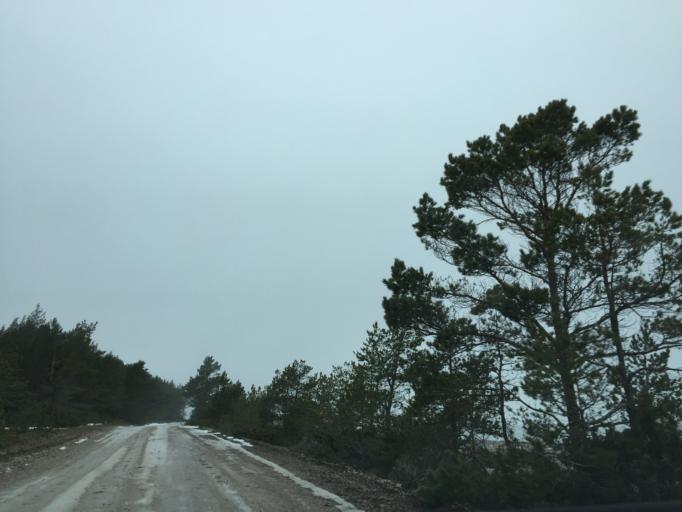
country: EE
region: Saare
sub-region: Kuressaare linn
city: Kuressaare
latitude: 58.5100
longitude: 21.9480
